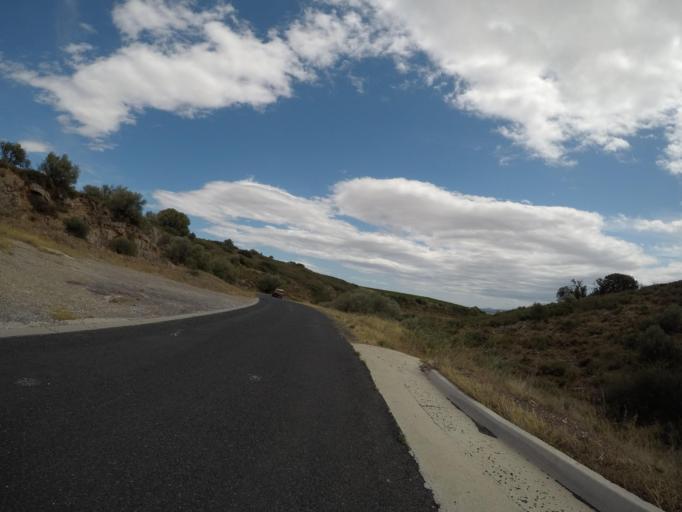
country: FR
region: Languedoc-Roussillon
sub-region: Departement des Pyrenees-Orientales
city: Baixas
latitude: 42.7538
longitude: 2.7752
